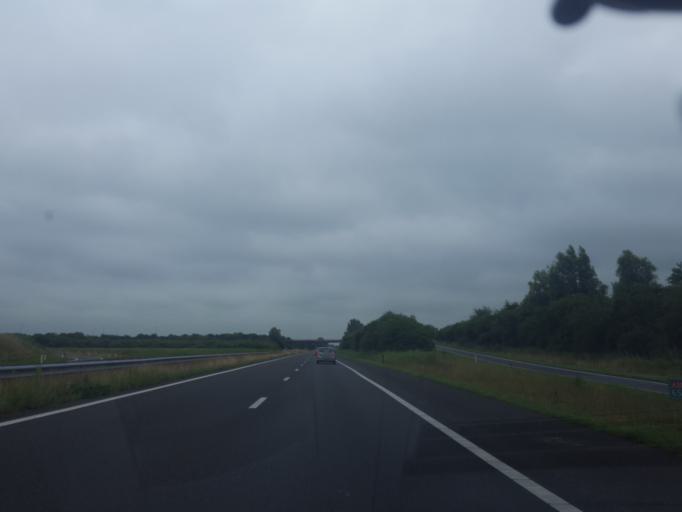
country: NL
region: Friesland
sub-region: Gemeente Boarnsterhim
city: Reduzum
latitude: 53.1158
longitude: 5.8108
